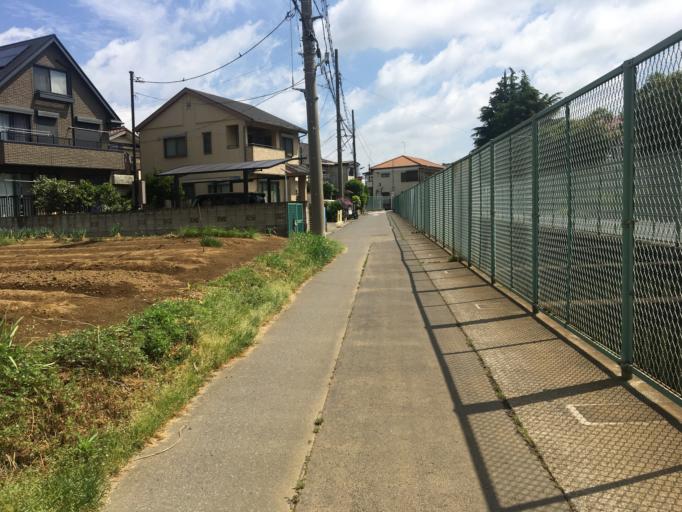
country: JP
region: Saitama
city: Yono
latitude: 35.8754
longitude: 139.6069
